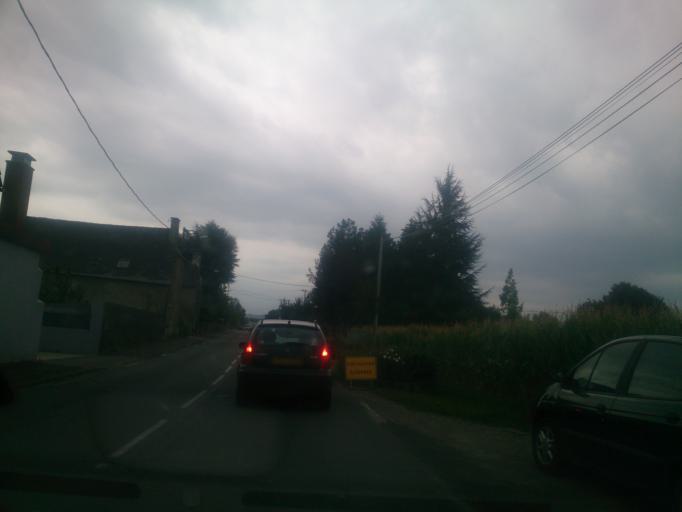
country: FR
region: Midi-Pyrenees
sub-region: Departement des Hautes-Pyrenees
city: Horgues
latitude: 43.1856
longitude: 0.0891
